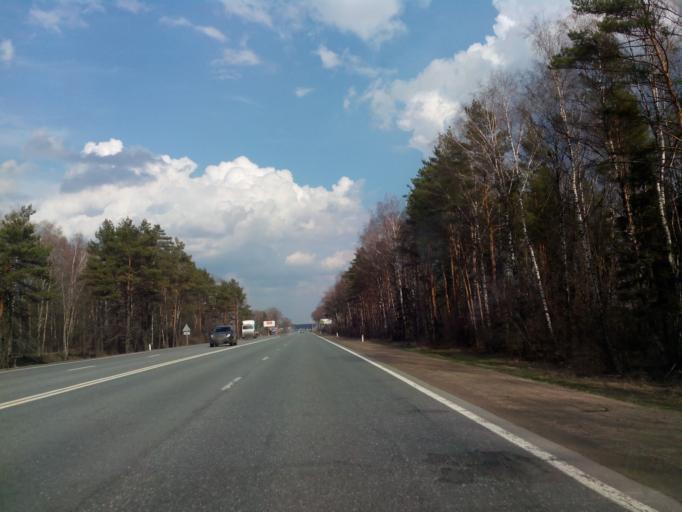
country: RU
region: Moskovskaya
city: Tuchkovo
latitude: 55.5551
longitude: 36.5356
